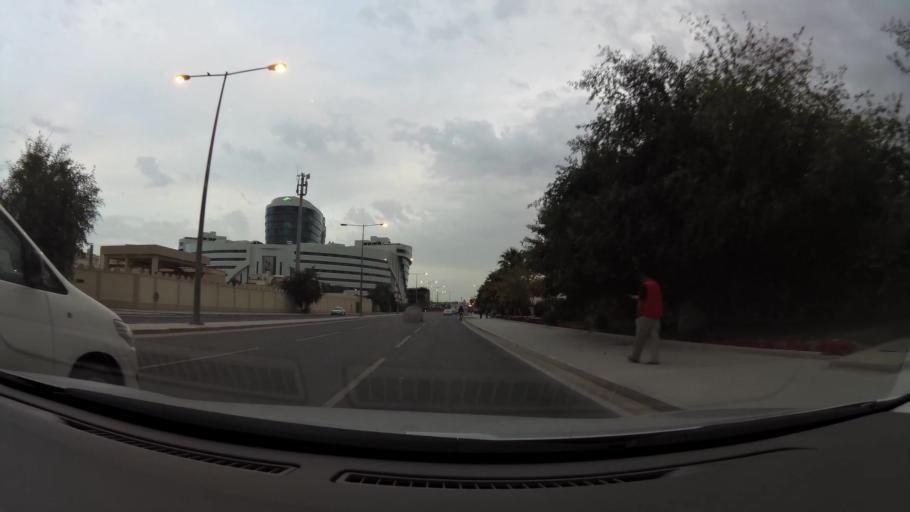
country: QA
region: Baladiyat ad Dawhah
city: Doha
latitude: 25.2668
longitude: 51.5257
